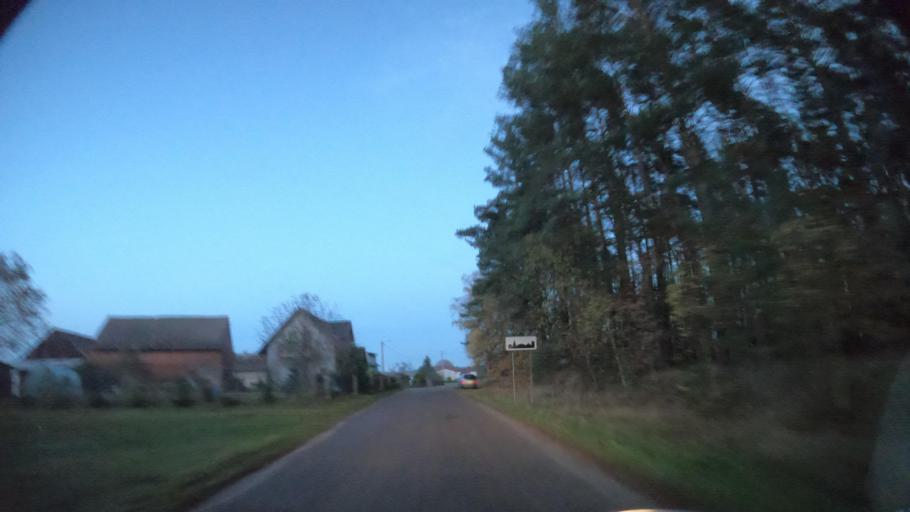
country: PL
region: Greater Poland Voivodeship
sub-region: Powiat zlotowski
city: Sypniewo
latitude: 53.4331
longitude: 16.6889
